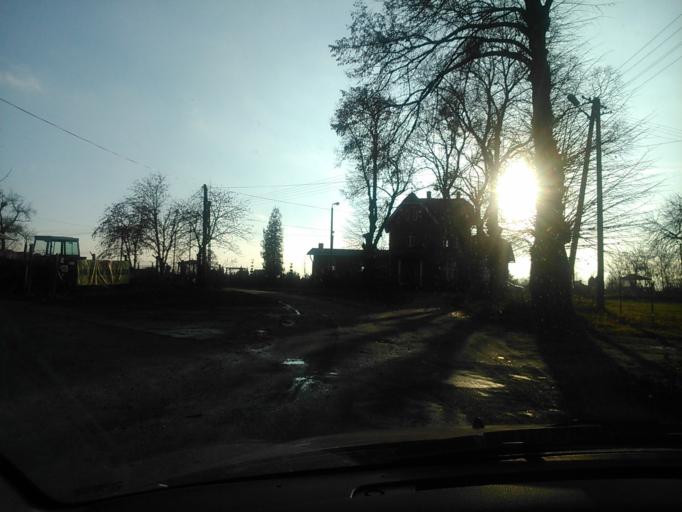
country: PL
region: Kujawsko-Pomorskie
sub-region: Powiat golubsko-dobrzynski
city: Golub-Dobrzyn
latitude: 53.1393
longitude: 18.9913
